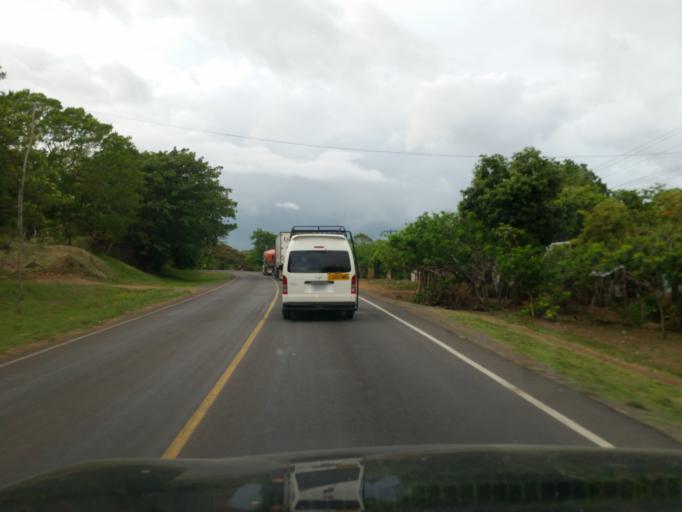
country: NI
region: Granada
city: Nandaime
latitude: 11.7253
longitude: -86.0126
